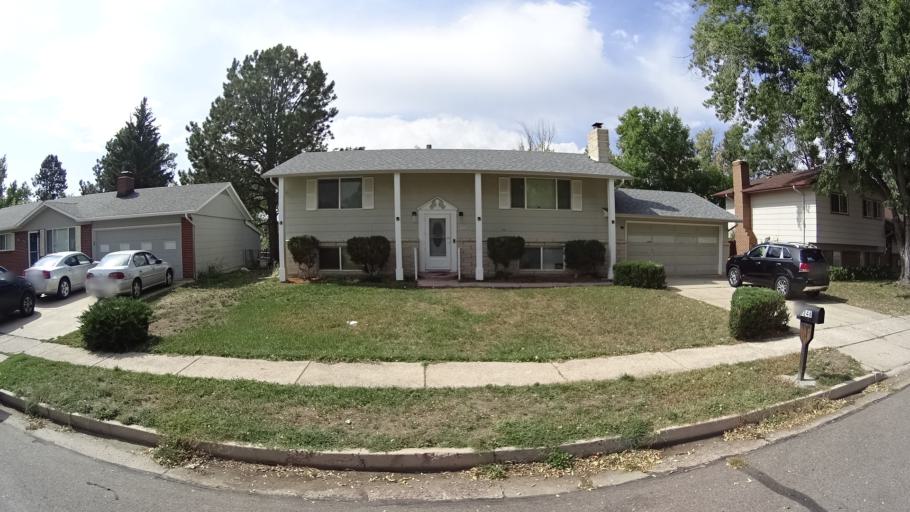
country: US
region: Colorado
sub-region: El Paso County
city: Cimarron Hills
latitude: 38.8513
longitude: -104.7414
